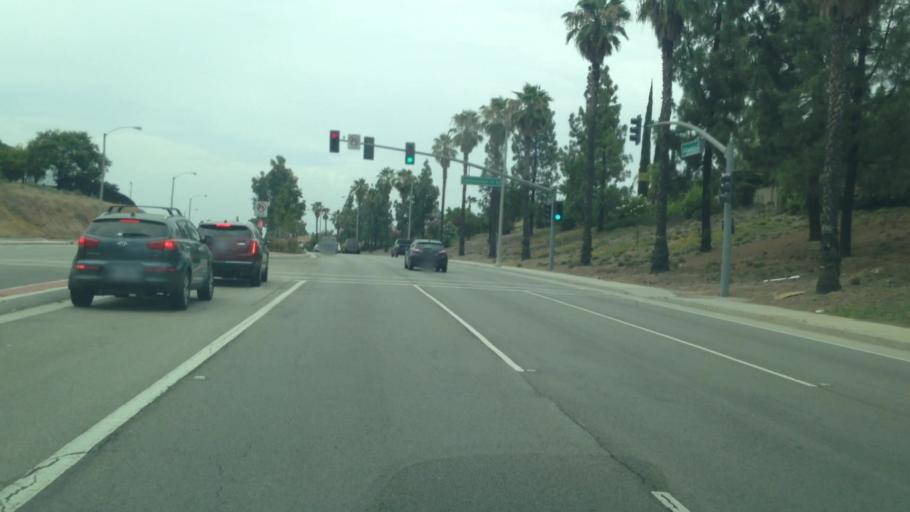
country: US
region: California
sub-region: Riverside County
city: Woodcrest
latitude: 33.9201
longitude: -117.3332
